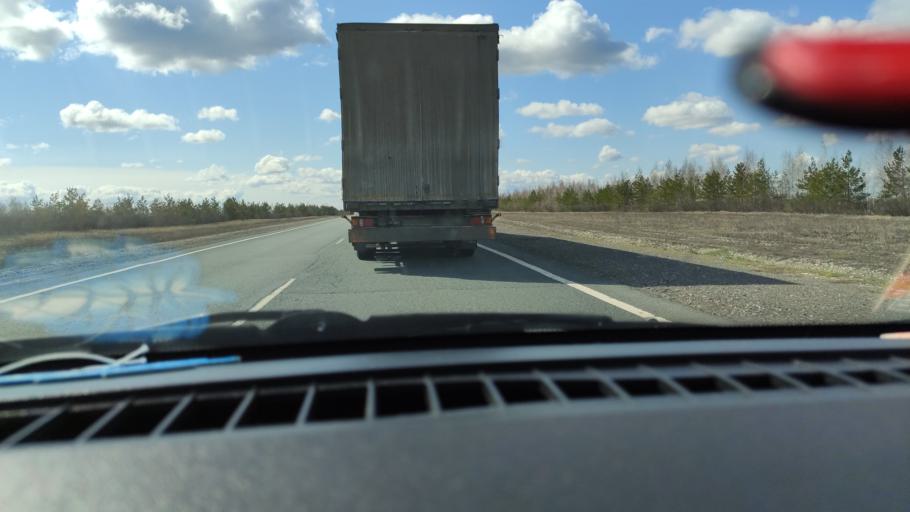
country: RU
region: Samara
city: Syzran'
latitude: 52.8798
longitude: 48.2920
